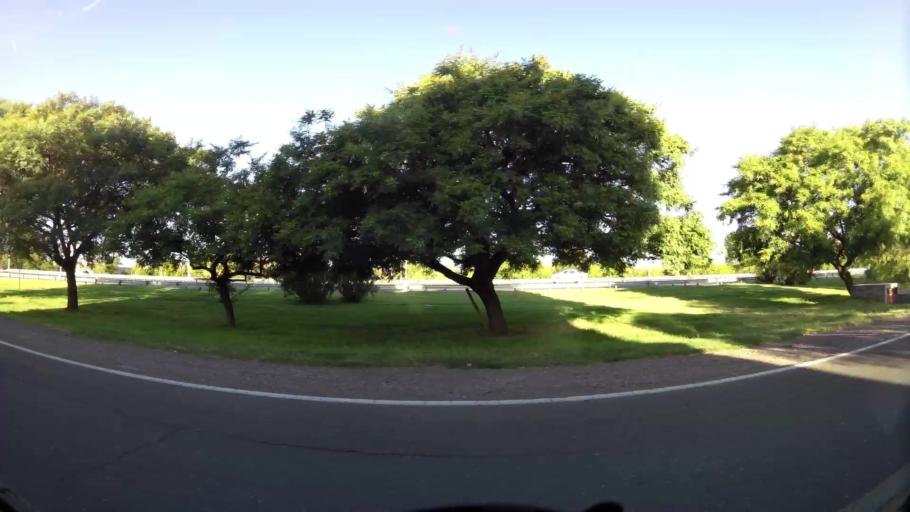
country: AR
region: San Juan
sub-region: Departamento de Santa Lucia
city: Santa Lucia
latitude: -31.5450
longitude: -68.5045
